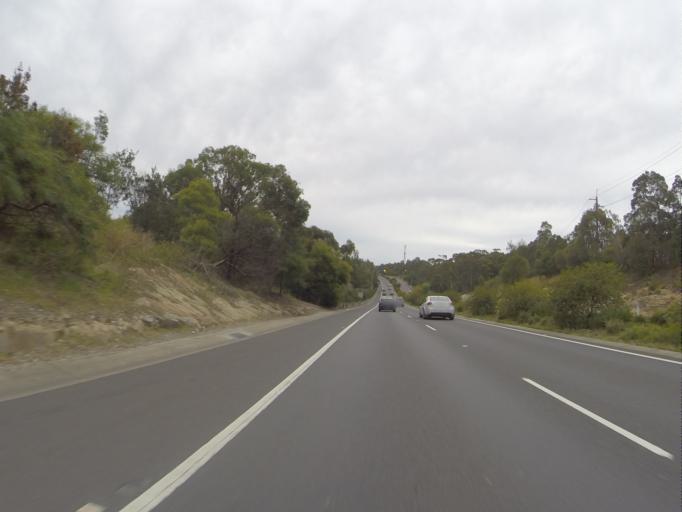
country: AU
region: New South Wales
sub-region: Sutherland Shire
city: Menai
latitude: -34.0160
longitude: 151.0095
